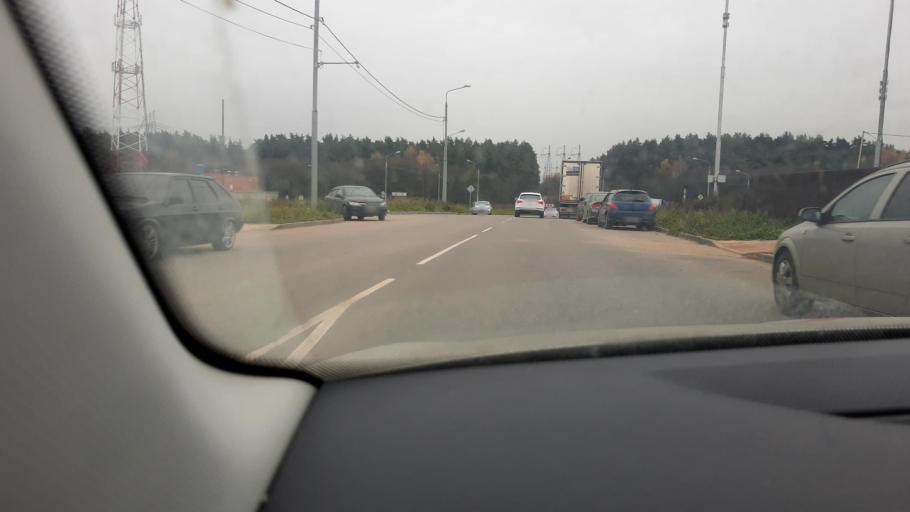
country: RU
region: Moscow
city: Annino
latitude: 55.5269
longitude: 37.6236
